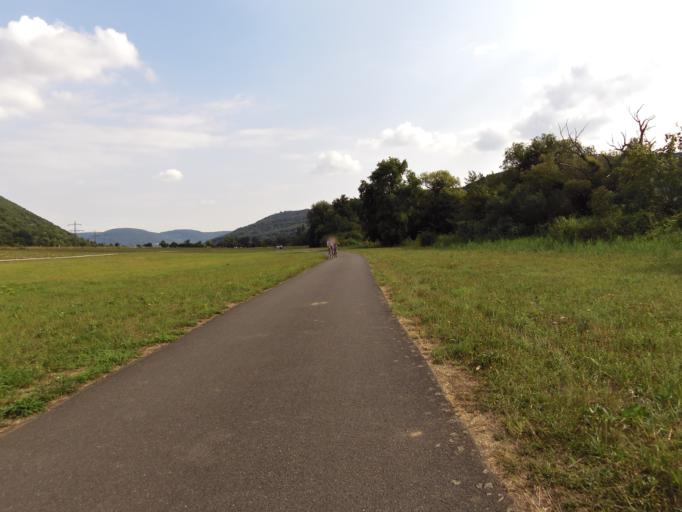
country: DE
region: Bavaria
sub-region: Regierungsbezirk Unterfranken
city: Laudenbach
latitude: 49.7478
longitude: 9.1797
